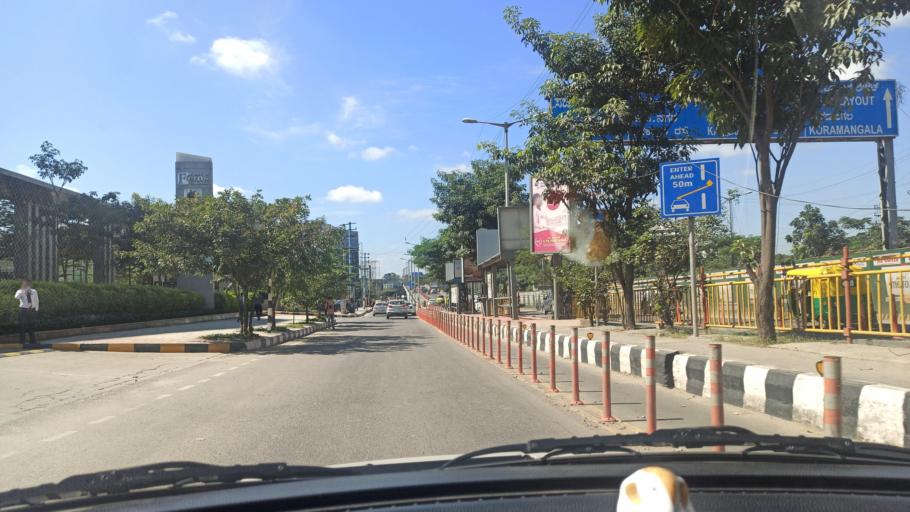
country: IN
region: Karnataka
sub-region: Bangalore Urban
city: Bangalore
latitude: 12.9222
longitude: 77.6689
